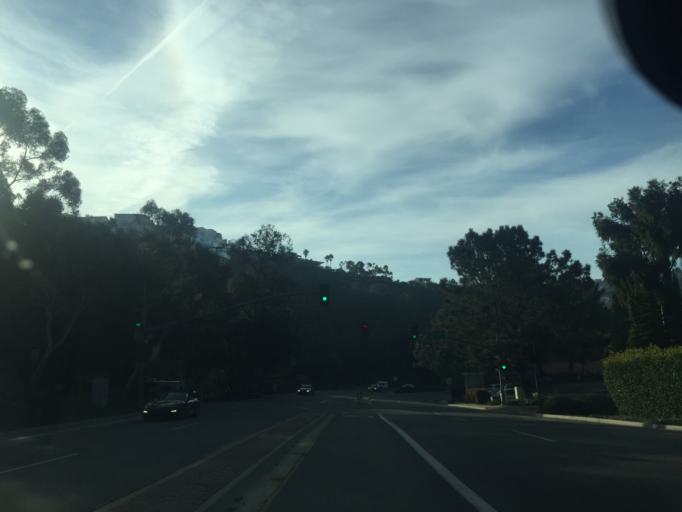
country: US
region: California
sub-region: San Diego County
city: La Jolla
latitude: 32.8538
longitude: -117.2454
